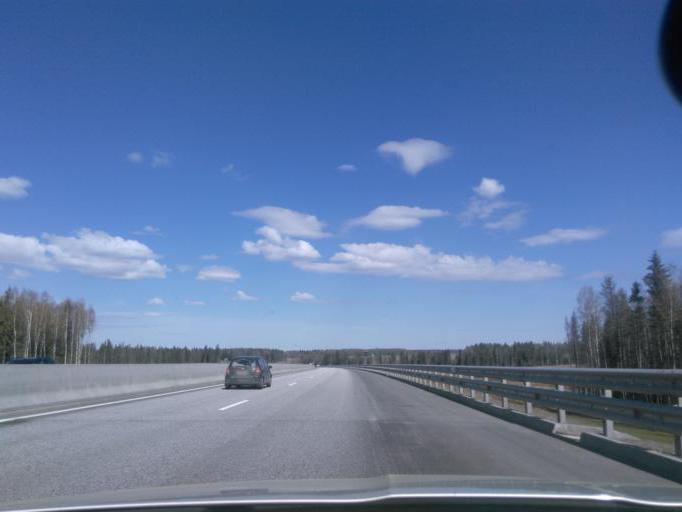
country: RU
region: Moskovskaya
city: Mendeleyevo
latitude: 56.0824
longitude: 37.2084
